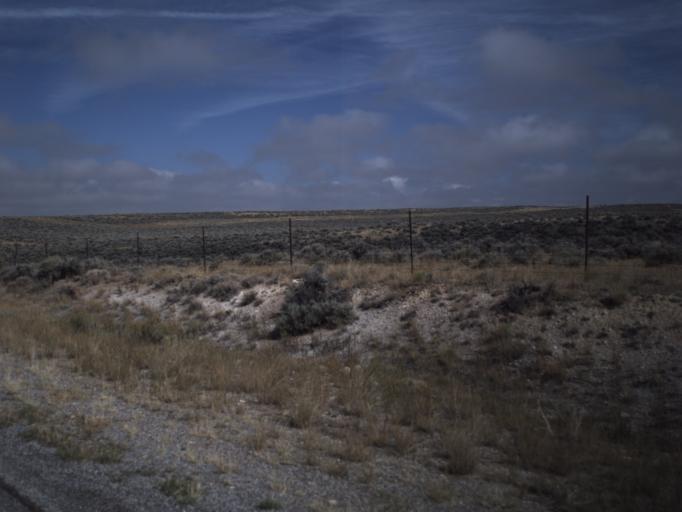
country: US
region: Wyoming
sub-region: Uinta County
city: Evanston
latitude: 41.4355
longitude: -111.0666
